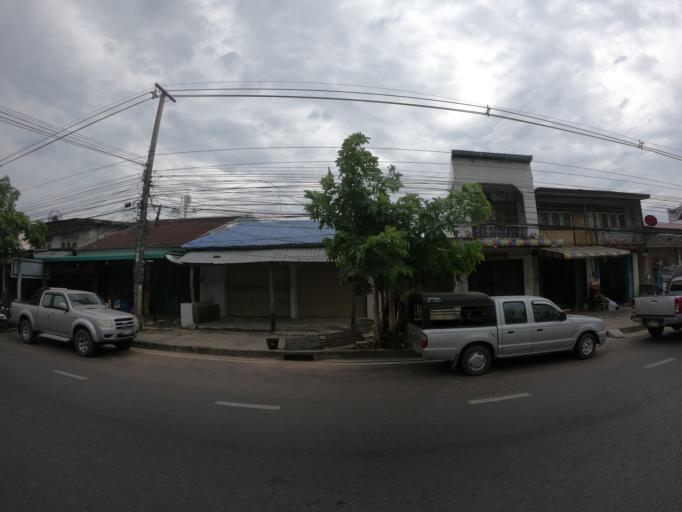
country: TH
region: Roi Et
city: Roi Et
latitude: 16.0615
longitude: 103.6608
